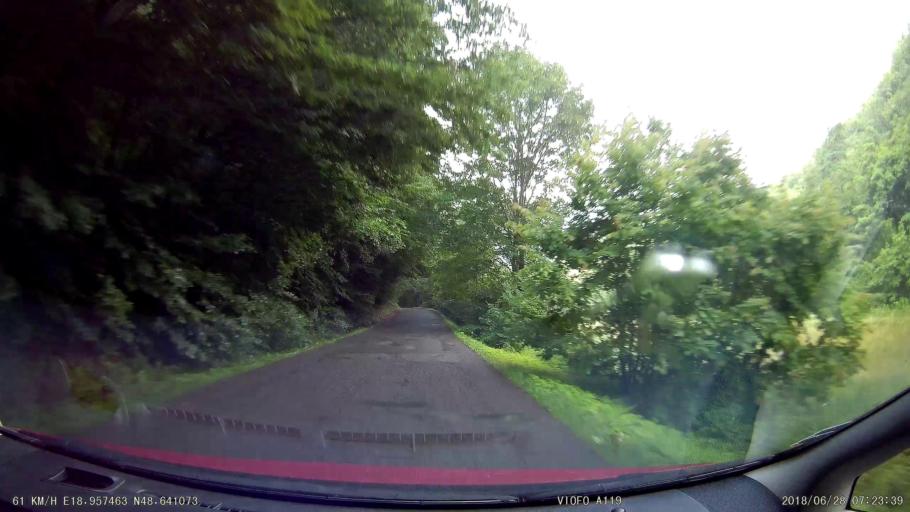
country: SK
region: Banskobystricky
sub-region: Okres Ziar nad Hronom
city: Kremnica
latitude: 48.6407
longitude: 18.9571
